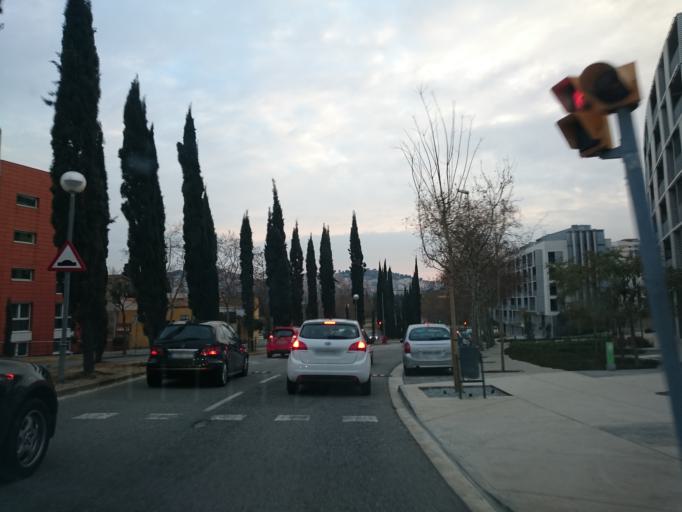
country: ES
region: Catalonia
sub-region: Provincia de Barcelona
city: Horta-Guinardo
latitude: 41.4356
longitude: 2.1535
